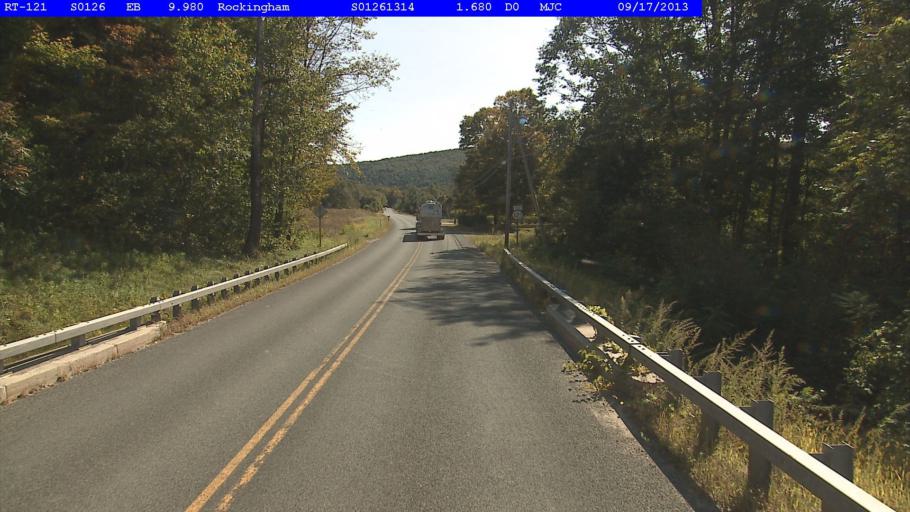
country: US
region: Vermont
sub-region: Windham County
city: Rockingham
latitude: 43.1386
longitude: -72.5309
